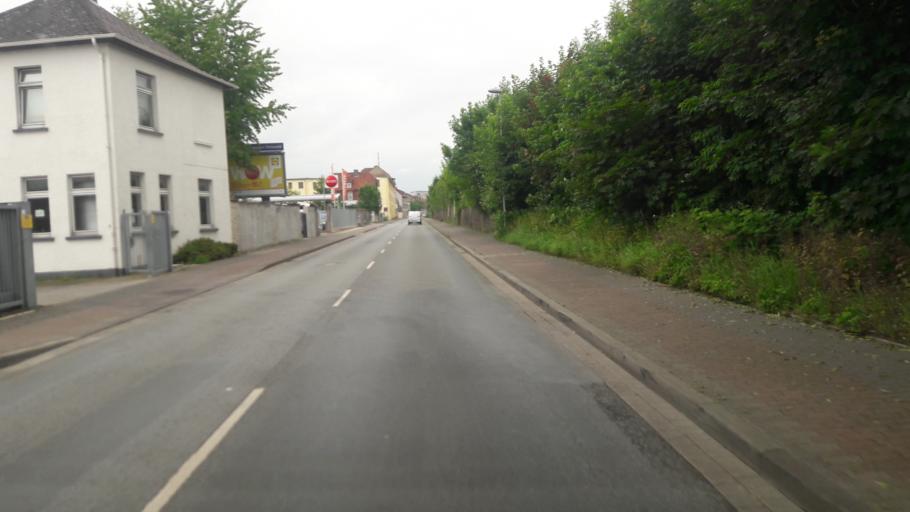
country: DE
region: North Rhine-Westphalia
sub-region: Regierungsbezirk Detmold
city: Detmold
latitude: 51.9428
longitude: 8.8679
